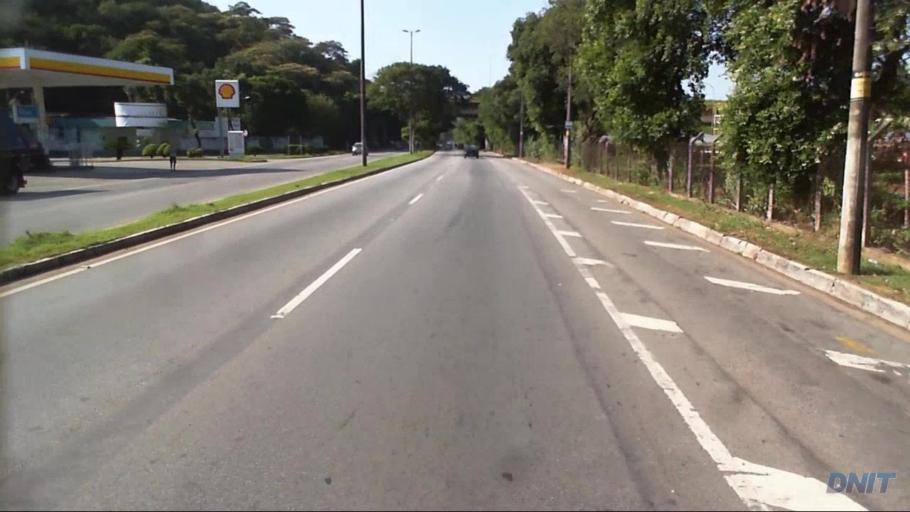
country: BR
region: Minas Gerais
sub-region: Ipatinga
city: Ipatinga
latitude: -19.5034
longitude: -42.5678
